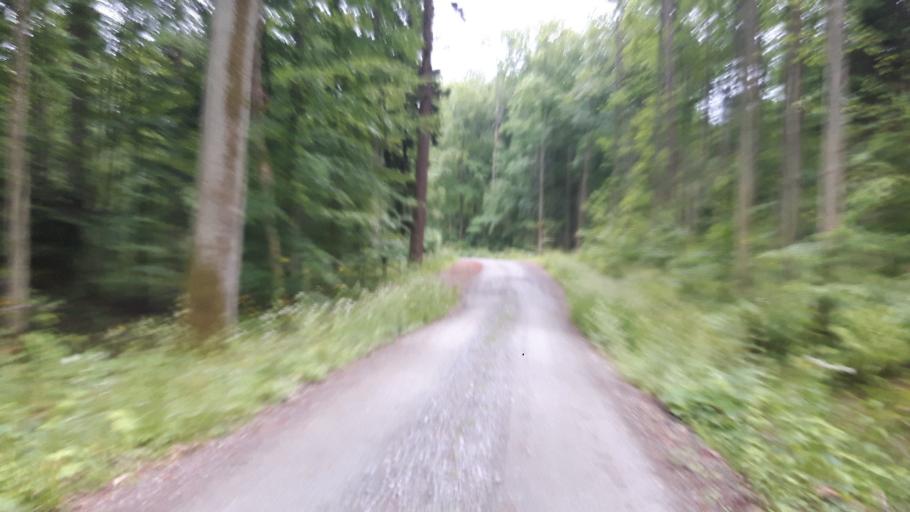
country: PL
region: Warmian-Masurian Voivodeship
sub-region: Powiat elblaski
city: Tolkmicko
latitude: 54.3307
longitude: 19.5924
